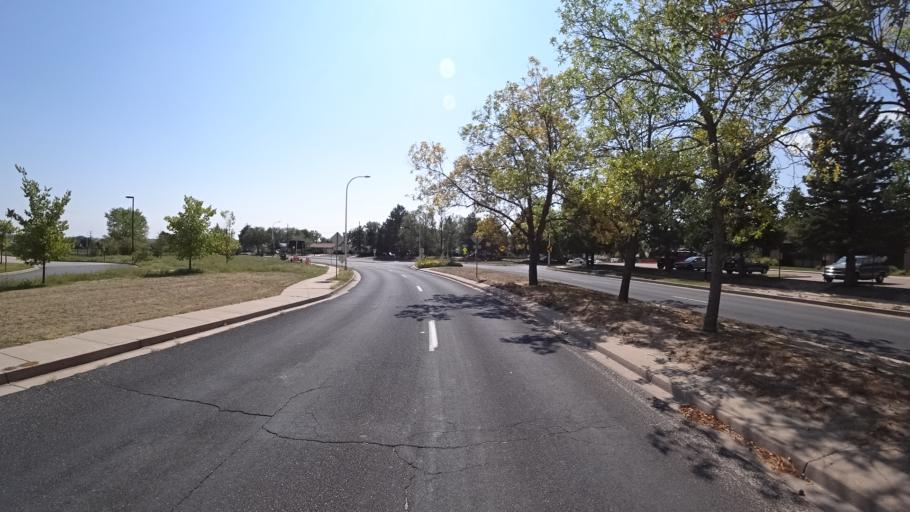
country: US
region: Colorado
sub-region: El Paso County
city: Colorado Springs
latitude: 38.8262
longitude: -104.7860
